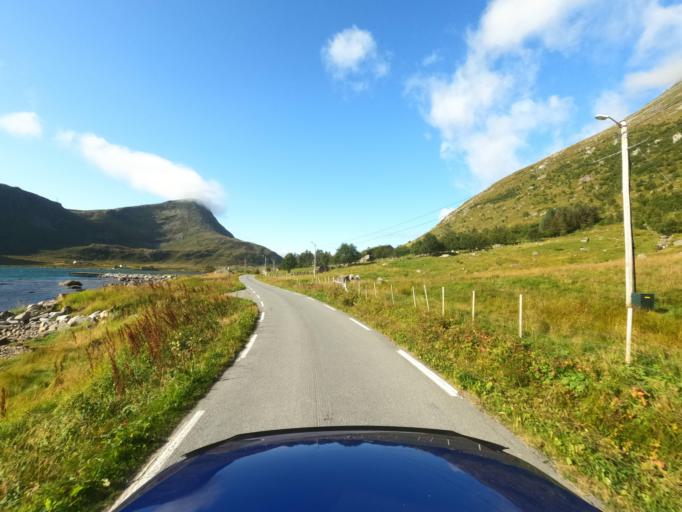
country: NO
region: Nordland
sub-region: Flakstad
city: Ramberg
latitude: 68.0544
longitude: 13.2501
